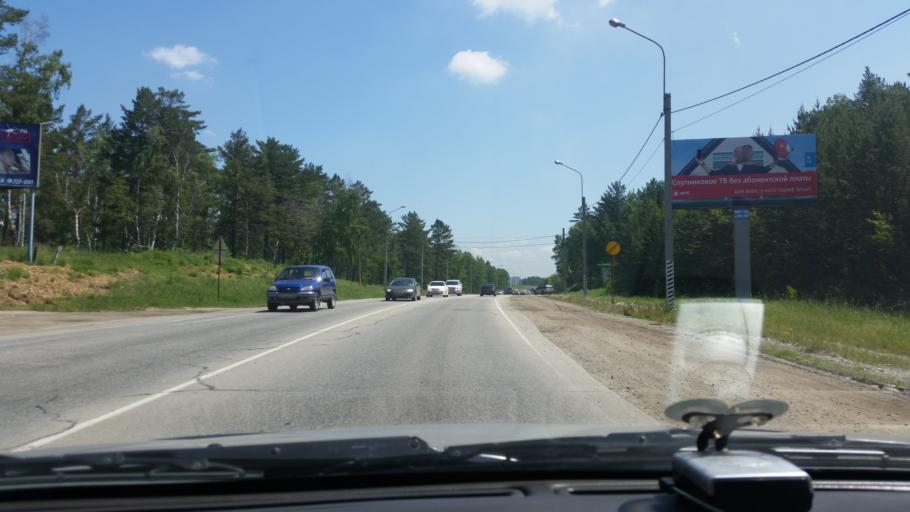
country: RU
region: Irkutsk
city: Smolenshchina
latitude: 52.2523
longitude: 104.1613
